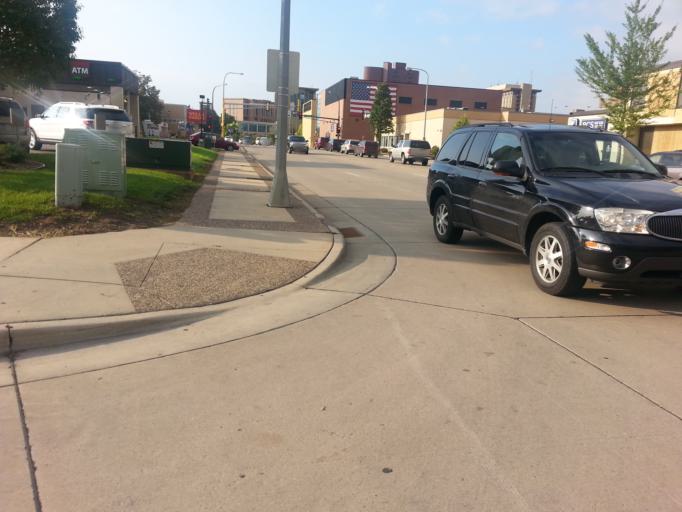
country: US
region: Minnesota
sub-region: Olmsted County
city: Rochester
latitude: 44.0244
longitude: -92.4600
